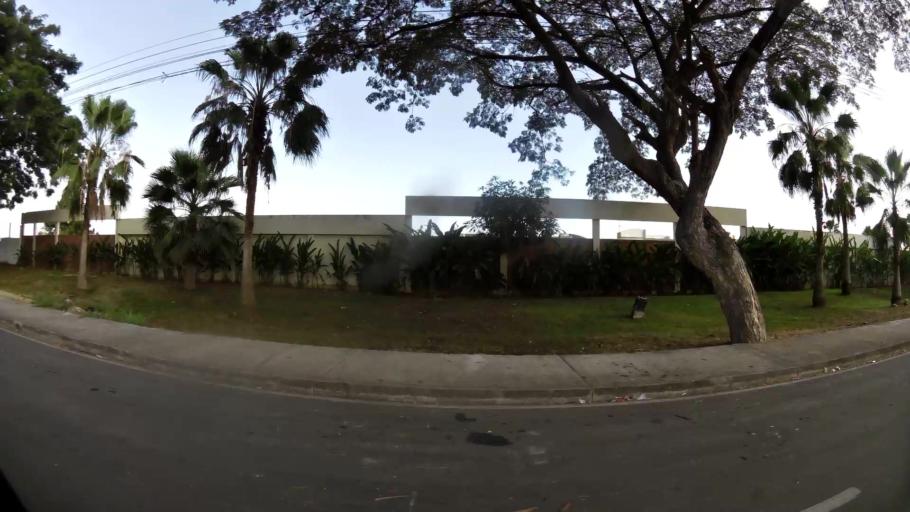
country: EC
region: Guayas
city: Santa Lucia
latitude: -2.1842
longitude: -79.9810
